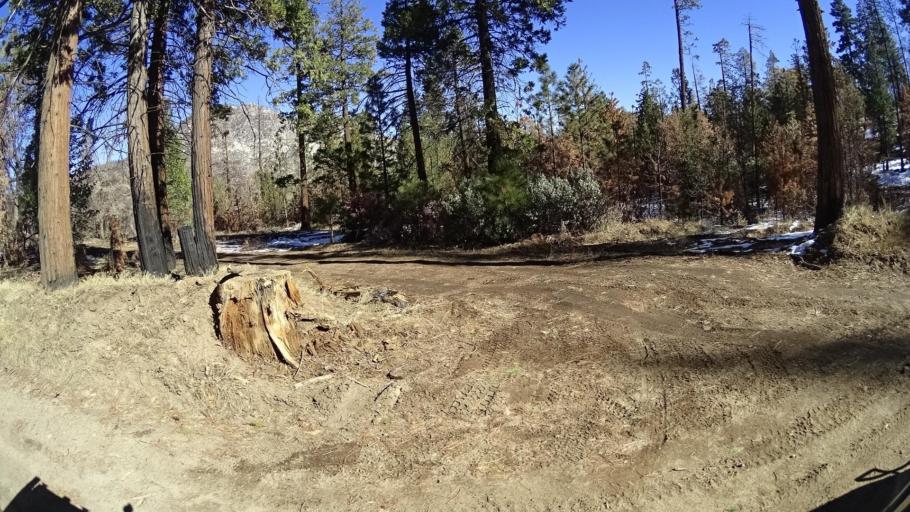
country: US
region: California
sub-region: Kern County
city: Alta Sierra
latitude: 35.7157
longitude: -118.5354
